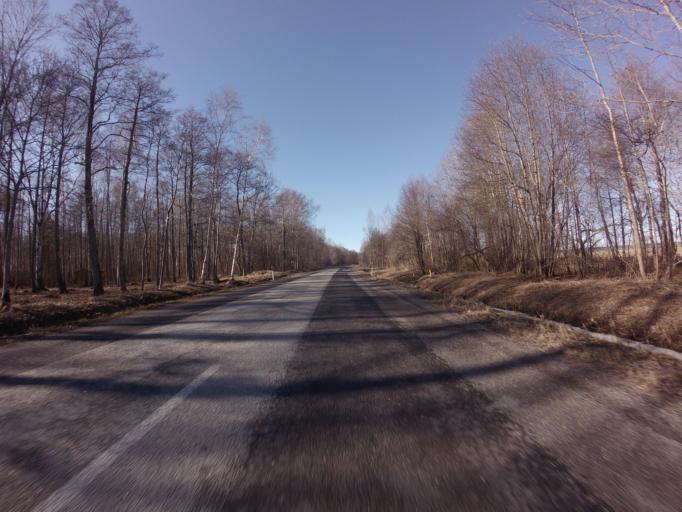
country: EE
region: Saare
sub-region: Kuressaare linn
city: Kuressaare
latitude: 58.5805
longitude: 22.6261
